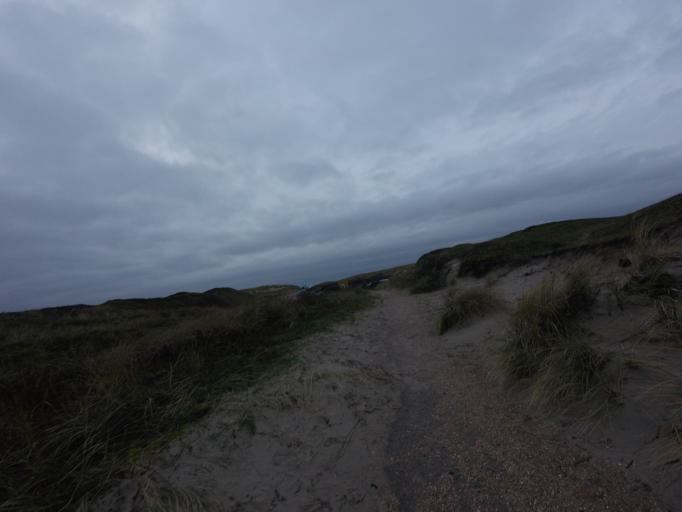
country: NL
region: North Holland
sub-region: Gemeente Texel
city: Den Burg
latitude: 53.0806
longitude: 4.7418
